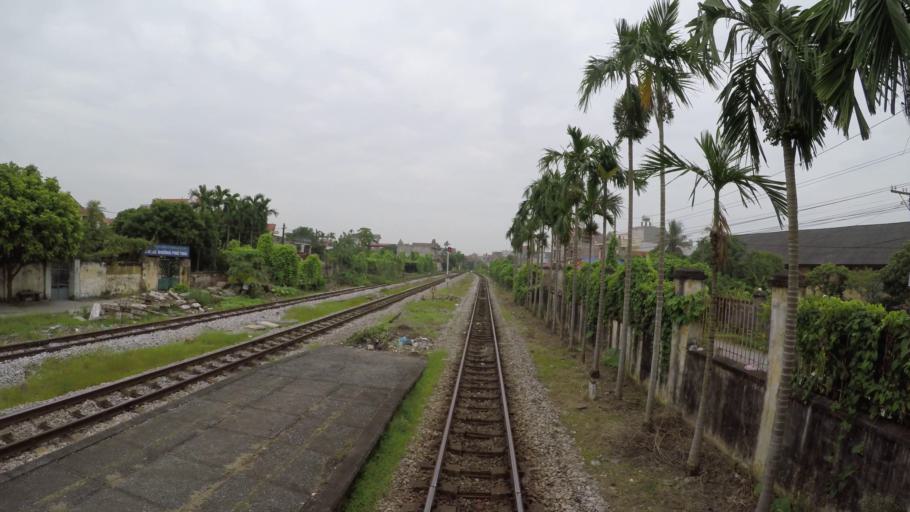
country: VN
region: Hai Duong
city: Phu Thai
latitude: 20.9703
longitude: 106.4965
